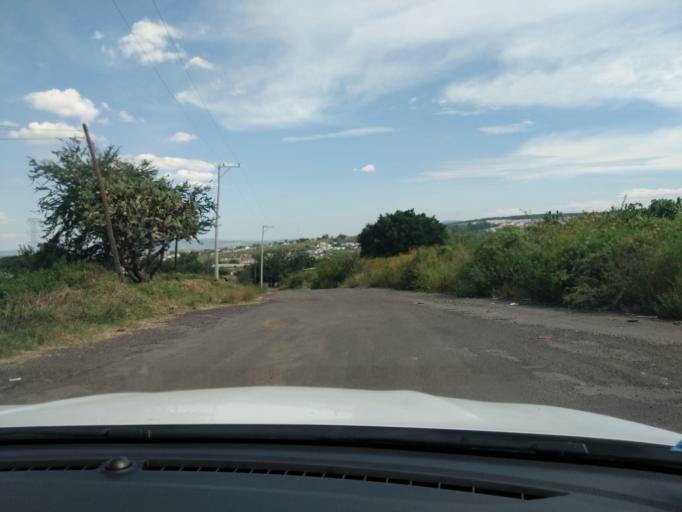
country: MX
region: Jalisco
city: Tonala
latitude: 20.6293
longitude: -103.2178
